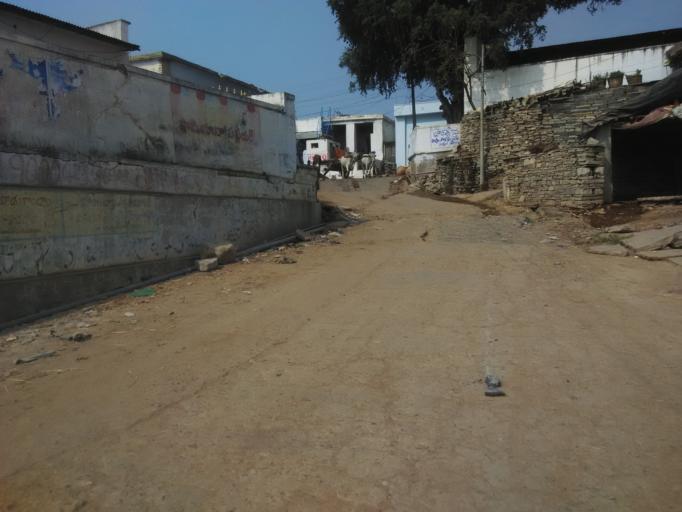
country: IN
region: Andhra Pradesh
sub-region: Kurnool
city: Nandyal
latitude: 15.4499
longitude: 78.4200
